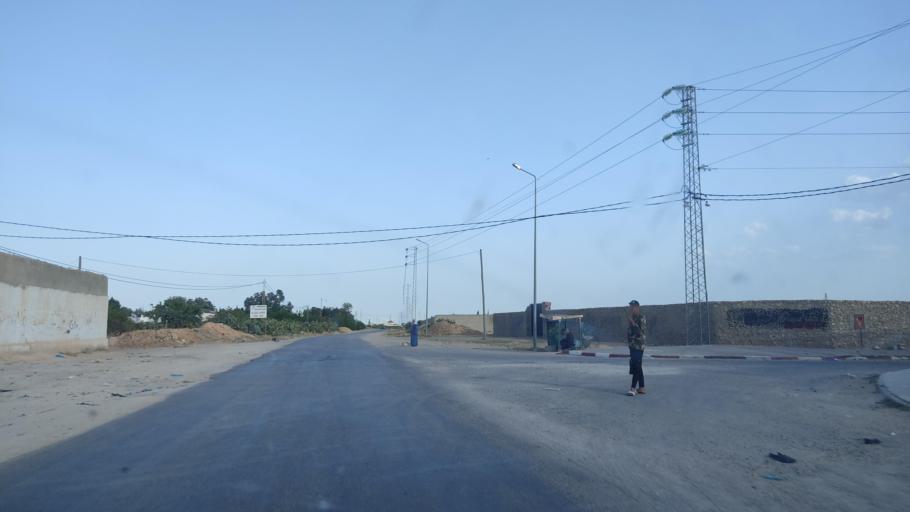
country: TN
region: Safaqis
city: Sfax
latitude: 34.8095
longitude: 10.6641
